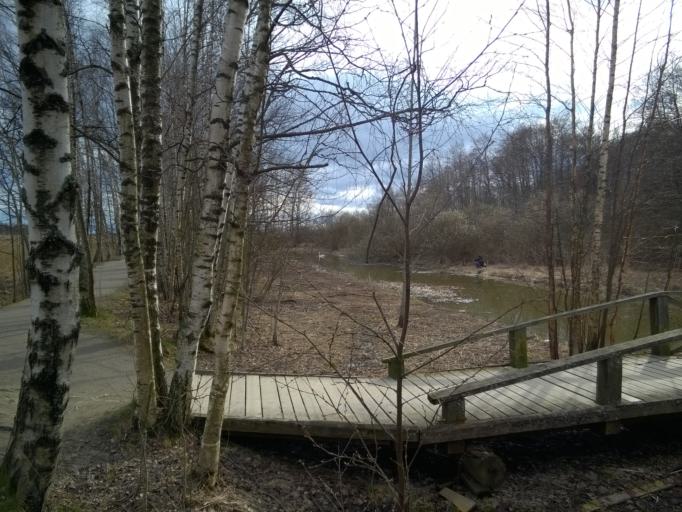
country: FI
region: Uusimaa
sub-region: Helsinki
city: Helsinki
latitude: 60.2148
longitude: 24.9925
